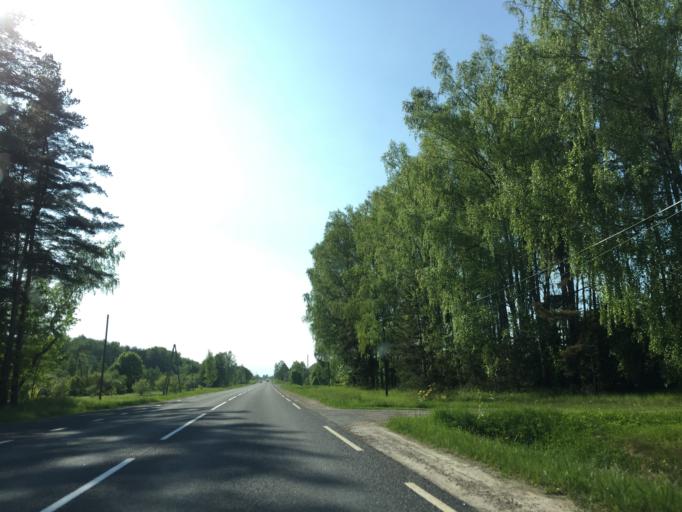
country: LV
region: Salaspils
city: Salaspils
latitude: 56.8224
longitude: 24.3938
